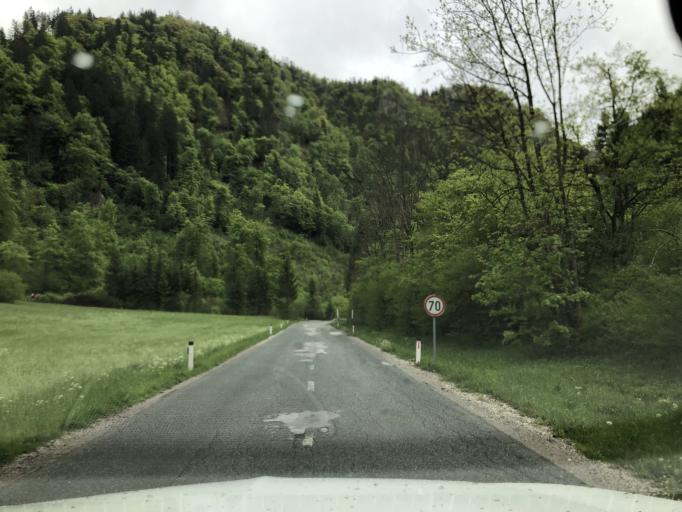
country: SI
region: Jesenice
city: Slovenski Javornik
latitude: 46.4059
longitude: 14.0785
